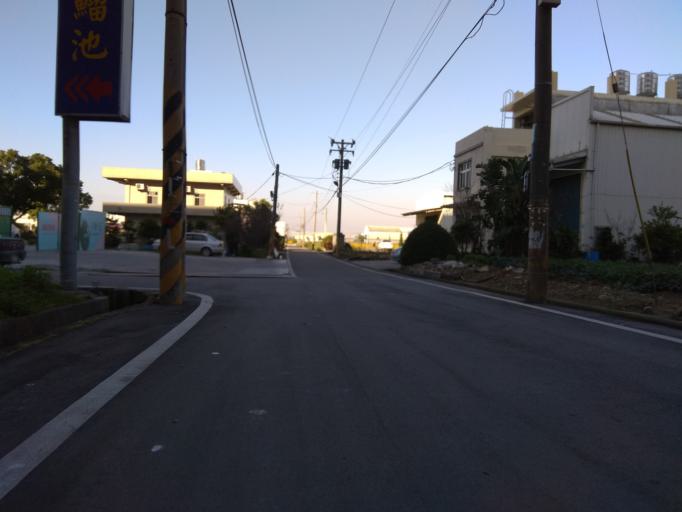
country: TW
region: Taiwan
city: Taoyuan City
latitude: 25.0074
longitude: 121.2263
